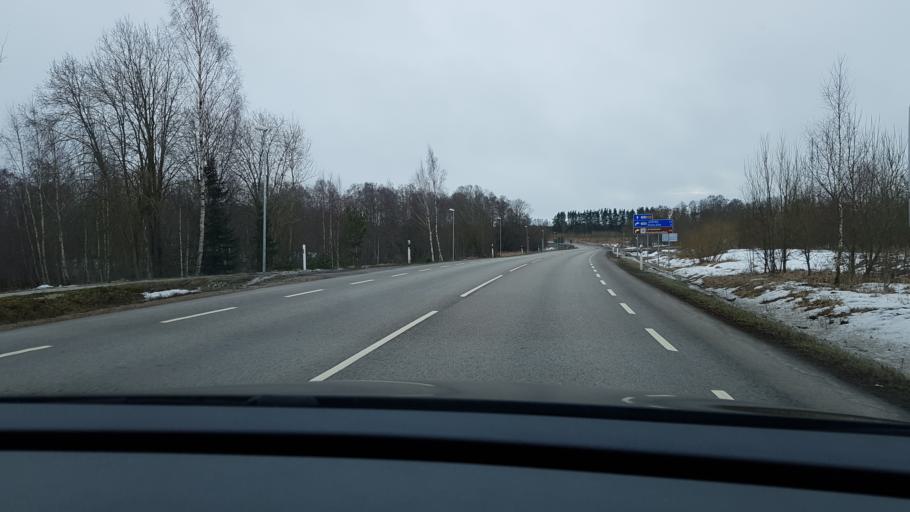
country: EE
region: Paernumaa
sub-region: Sauga vald
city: Sauga
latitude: 58.4266
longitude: 24.4403
